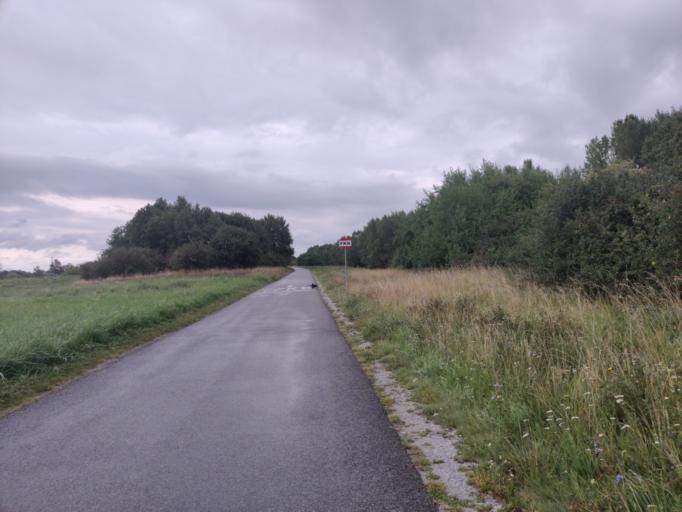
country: AT
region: Lower Austria
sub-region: Politischer Bezirk Korneuburg
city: Langenzersdorf
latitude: 48.2821
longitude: 16.3577
